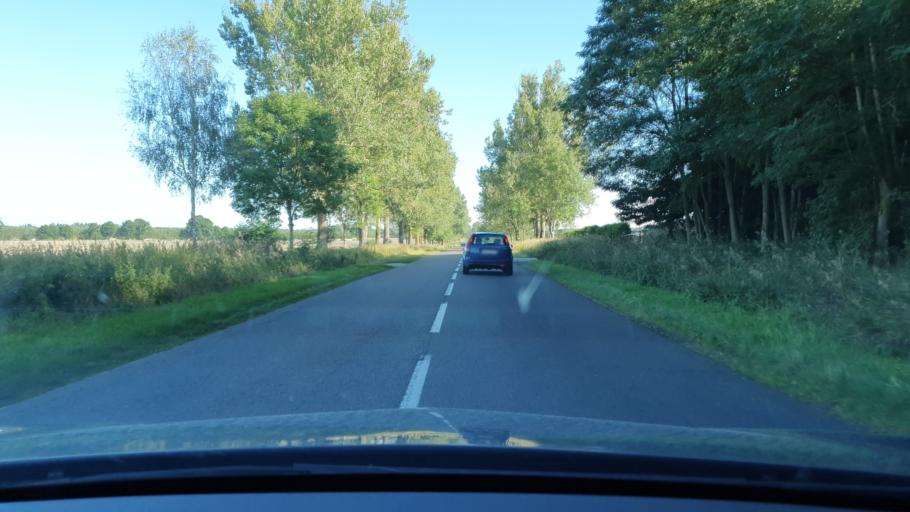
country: PL
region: West Pomeranian Voivodeship
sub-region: Powiat goleniowski
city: Przybiernow
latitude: 53.8381
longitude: 14.7581
